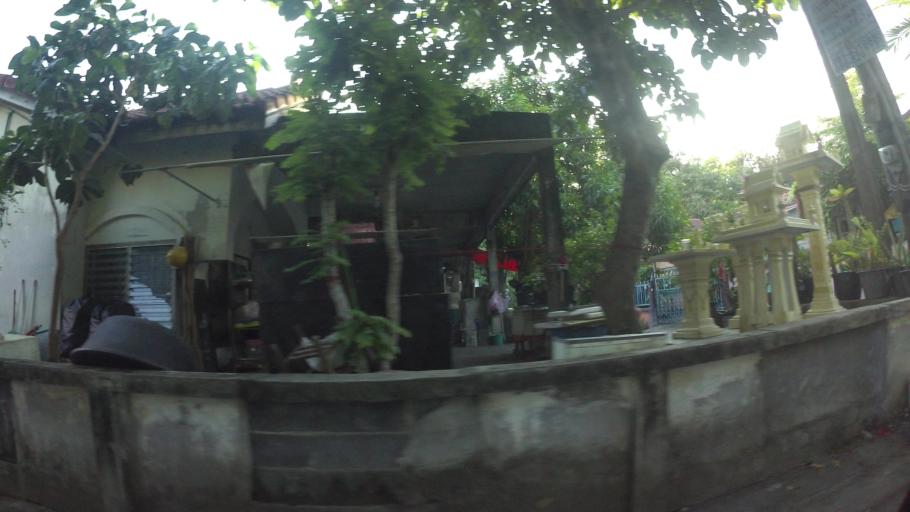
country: TH
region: Rayong
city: Rayong
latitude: 12.6871
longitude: 101.2777
